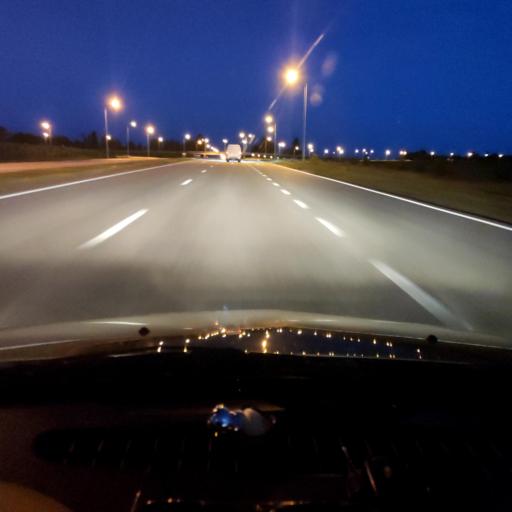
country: RU
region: Belgorod
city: Skorodnoye
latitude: 51.0588
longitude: 37.2028
